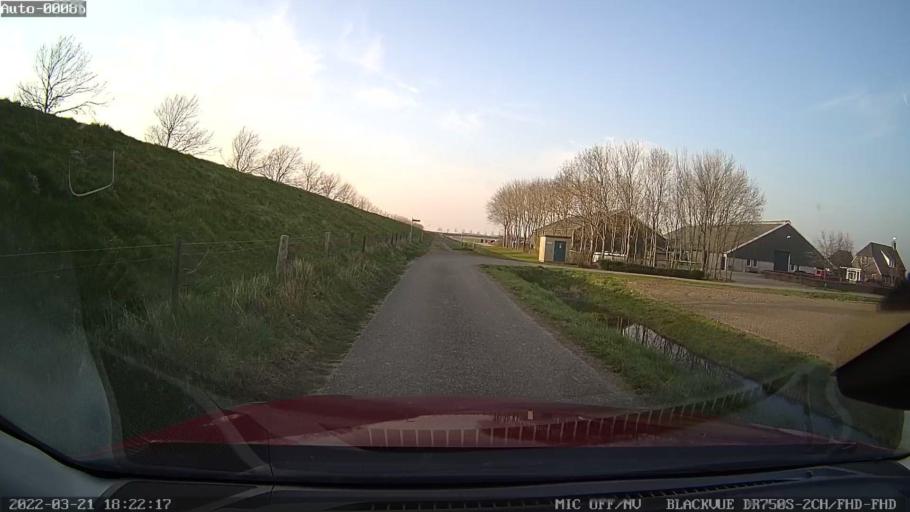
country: NL
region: North Brabant
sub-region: Gemeente Steenbergen
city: Nieuw-Vossemeer
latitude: 51.5897
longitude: 4.2028
